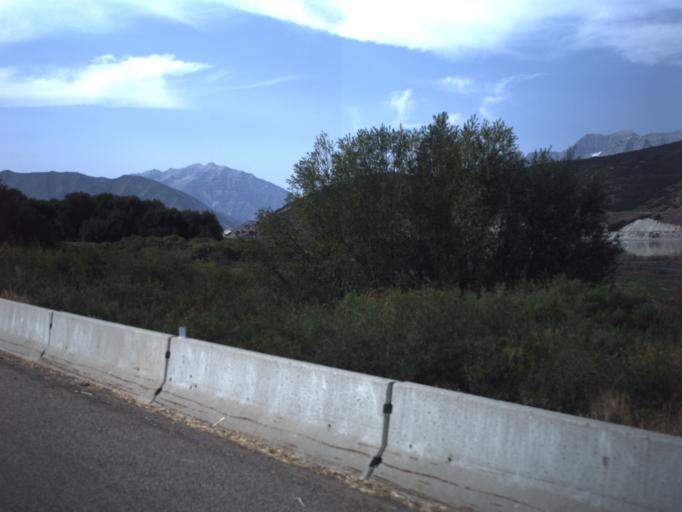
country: US
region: Utah
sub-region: Wasatch County
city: Midway
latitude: 40.4768
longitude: -111.4719
